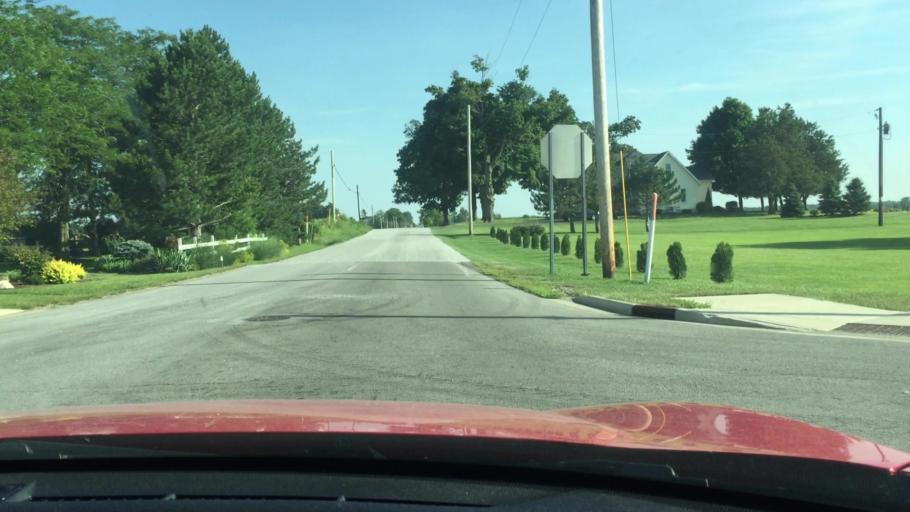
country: US
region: Ohio
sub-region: Hardin County
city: Ada
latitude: 40.7619
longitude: -83.8424
